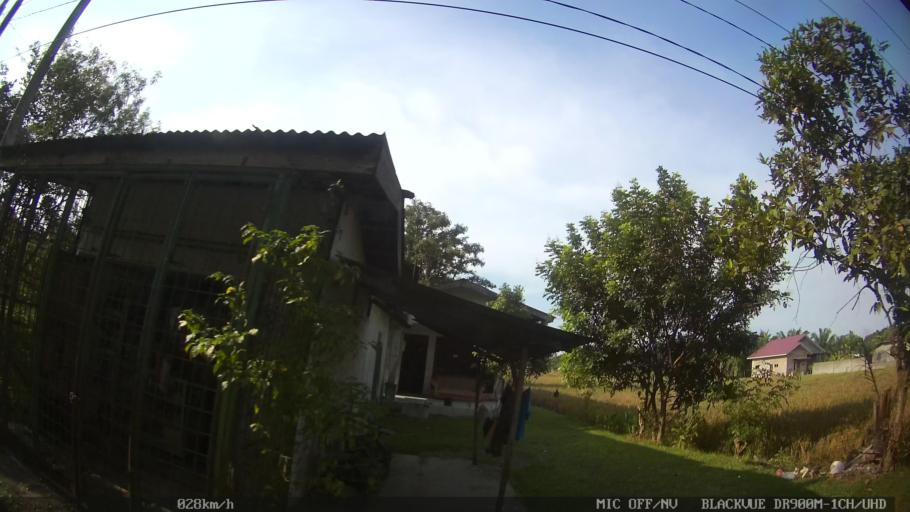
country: ID
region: North Sumatra
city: Binjai
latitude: 3.6210
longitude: 98.5208
